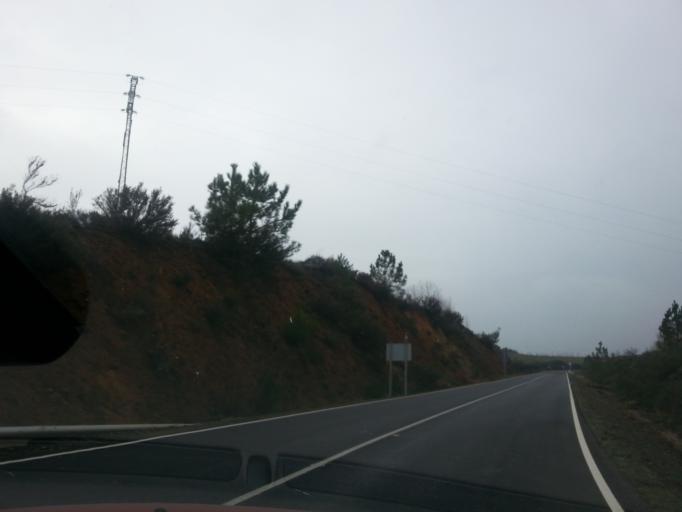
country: ES
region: Castille and Leon
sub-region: Provincia de Salamanca
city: Sotoserrano
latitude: 40.4375
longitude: -6.0409
